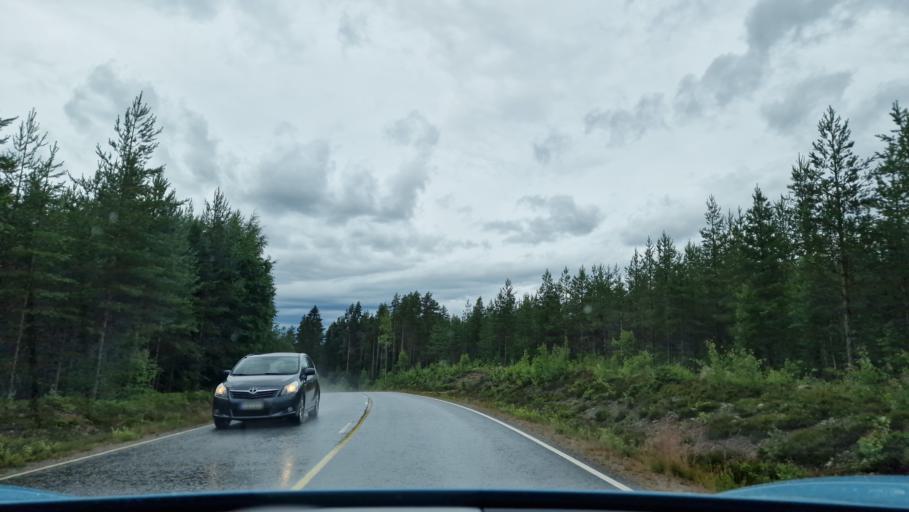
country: FI
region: Central Finland
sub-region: Saarijaervi-Viitasaari
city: Pylkoenmaeki
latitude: 62.6680
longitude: 24.5356
